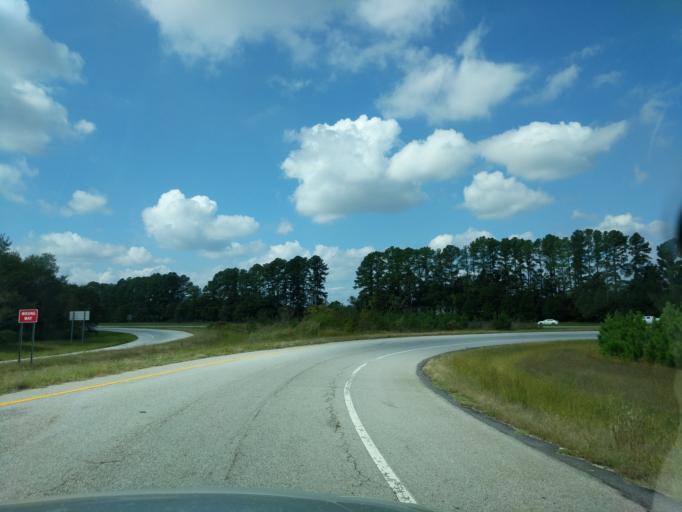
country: US
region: Georgia
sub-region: Hart County
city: Reed Creek
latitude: 34.5259
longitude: -82.8429
